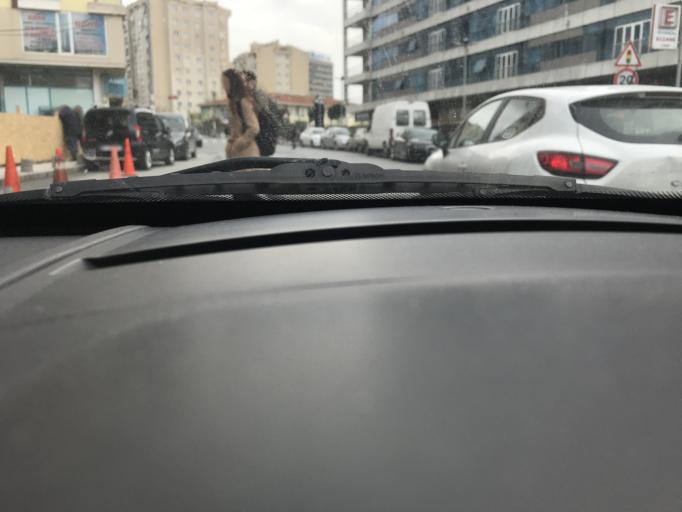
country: TR
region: Istanbul
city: Yakuplu
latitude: 41.0051
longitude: 28.6902
